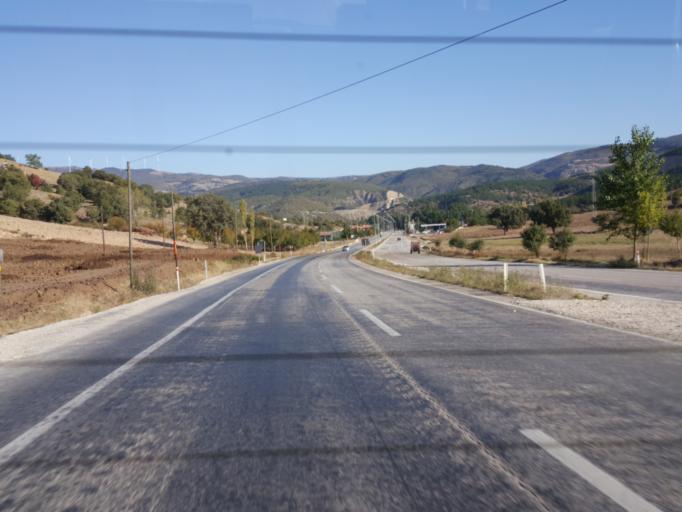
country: TR
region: Amasya
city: Ezinepazari
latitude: 40.5593
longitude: 36.1382
